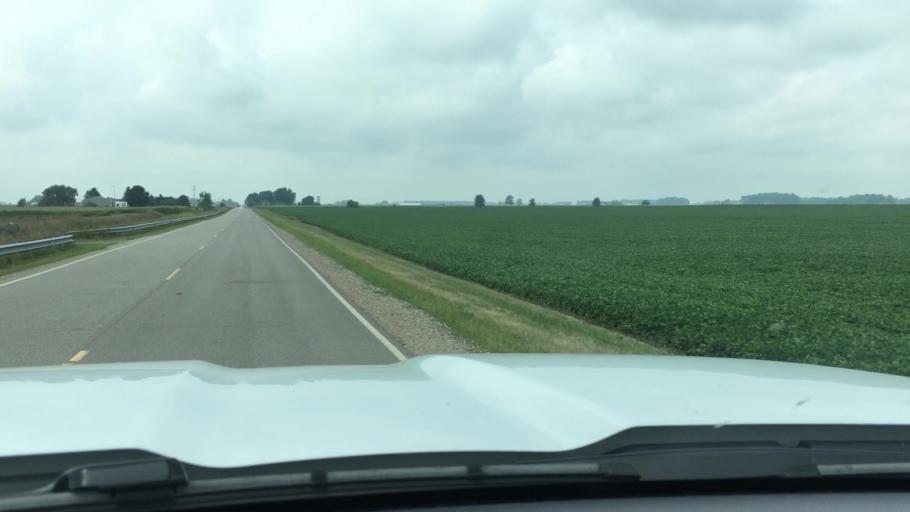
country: US
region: Michigan
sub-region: Sanilac County
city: Marlette
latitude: 43.3591
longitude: -82.9830
